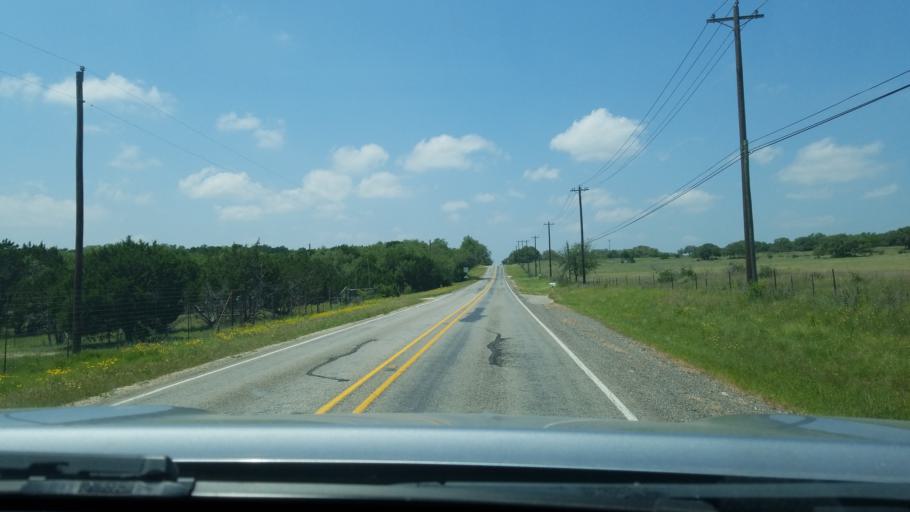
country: US
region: Texas
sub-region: Hays County
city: Woodcreek
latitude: 30.0377
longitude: -98.1849
